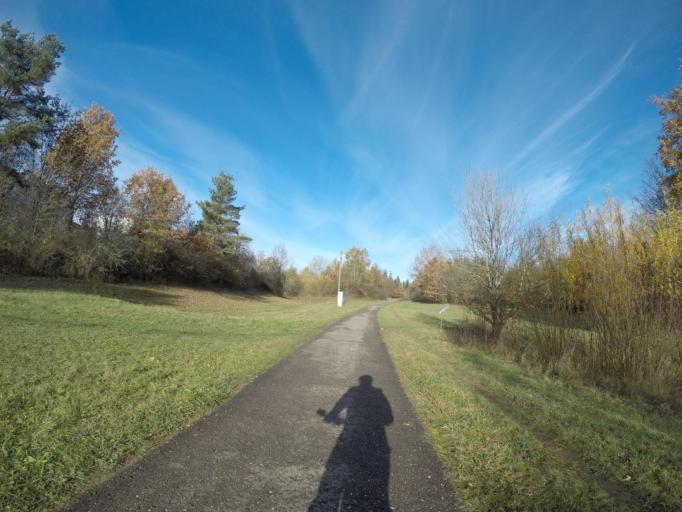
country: DE
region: Baden-Wuerttemberg
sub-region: Tuebingen Region
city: Dornstadt
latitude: 48.4246
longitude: 9.9420
